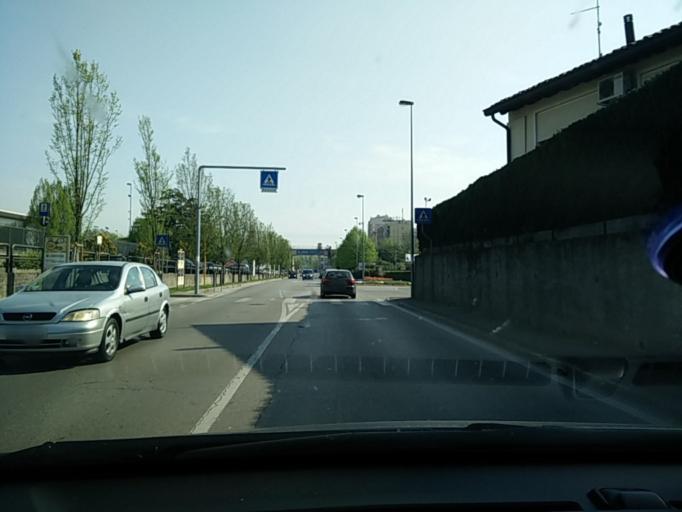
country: IT
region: Friuli Venezia Giulia
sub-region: Provincia di Pordenone
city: Pordenone
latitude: 45.9486
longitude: 12.6579
